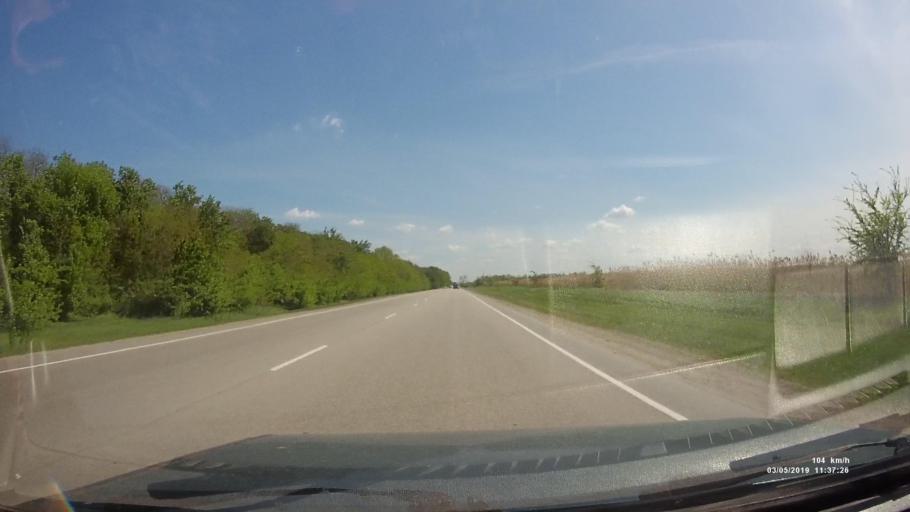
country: RU
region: Rostov
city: Ol'ginskaya
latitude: 47.1318
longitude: 39.9431
